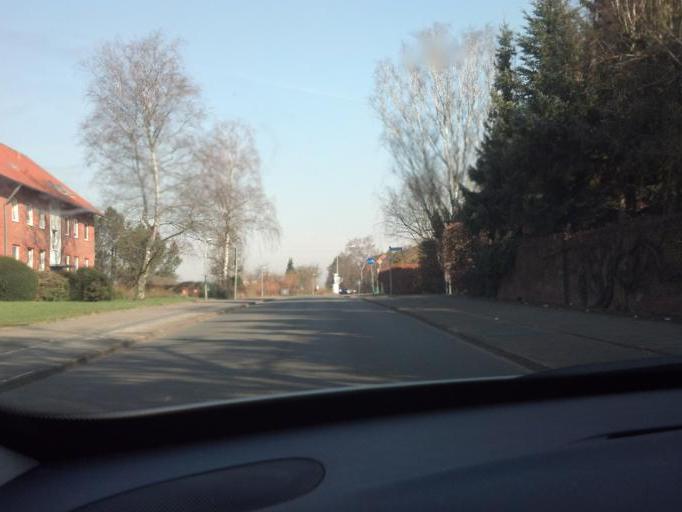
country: DE
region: Lower Saxony
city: Lueneburg
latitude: 53.2564
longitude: 10.3924
